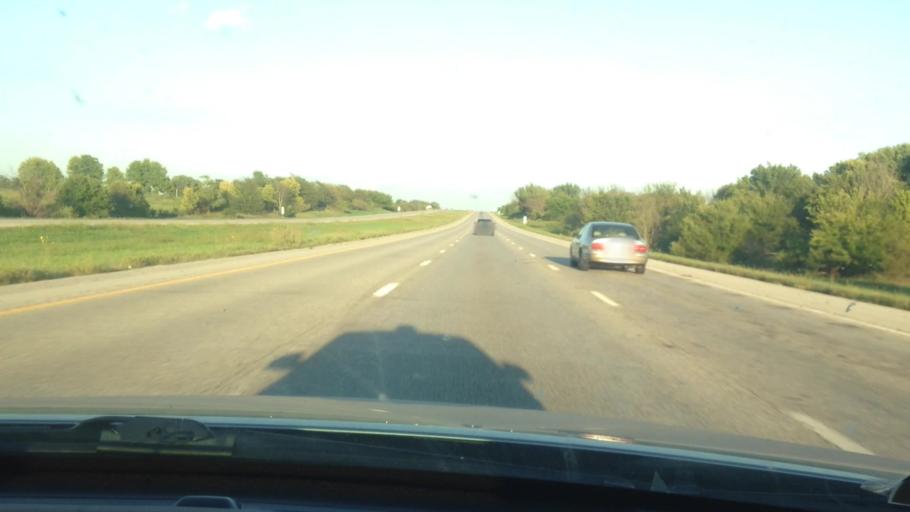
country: US
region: Missouri
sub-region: Clay County
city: Smithville
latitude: 39.3073
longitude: -94.6315
